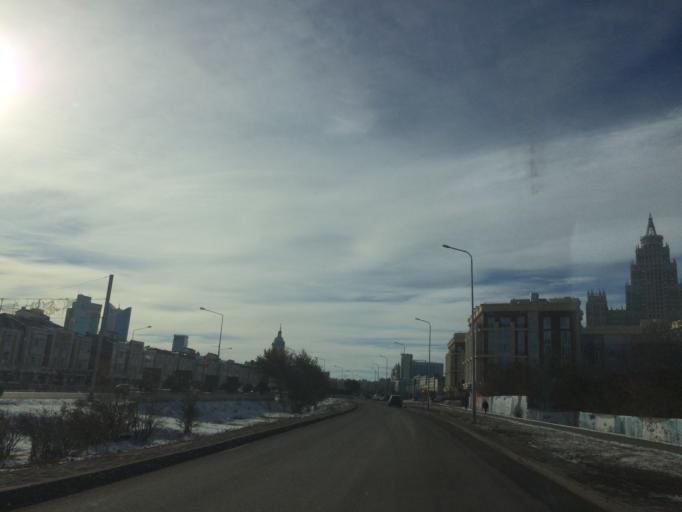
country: KZ
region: Astana Qalasy
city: Astana
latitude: 51.1435
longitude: 71.4196
